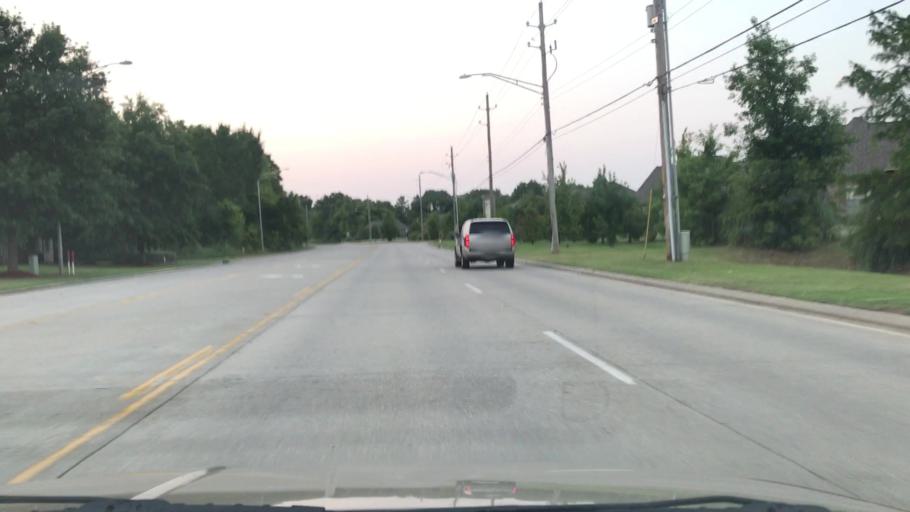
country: US
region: Louisiana
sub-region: Bossier Parish
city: Bossier City
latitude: 32.4318
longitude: -93.7259
